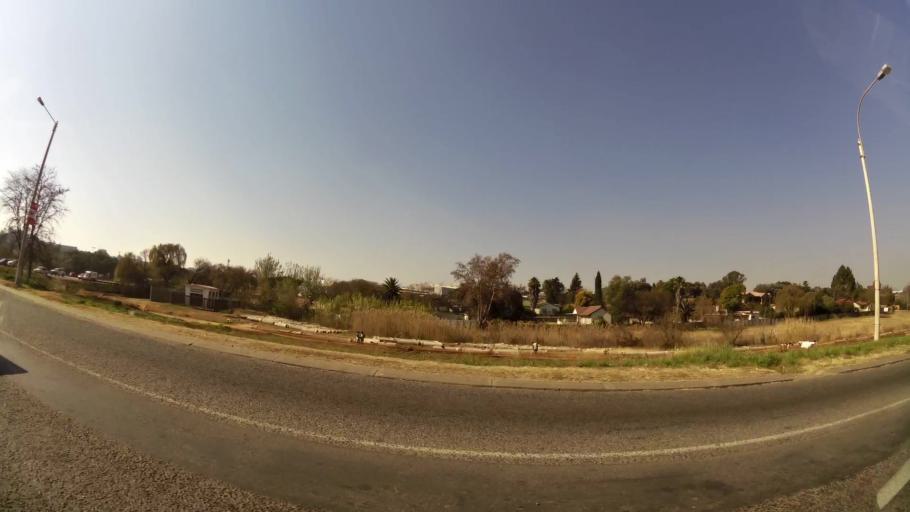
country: ZA
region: Gauteng
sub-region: City of Johannesburg Metropolitan Municipality
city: Modderfontein
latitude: -26.1076
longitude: 28.1678
